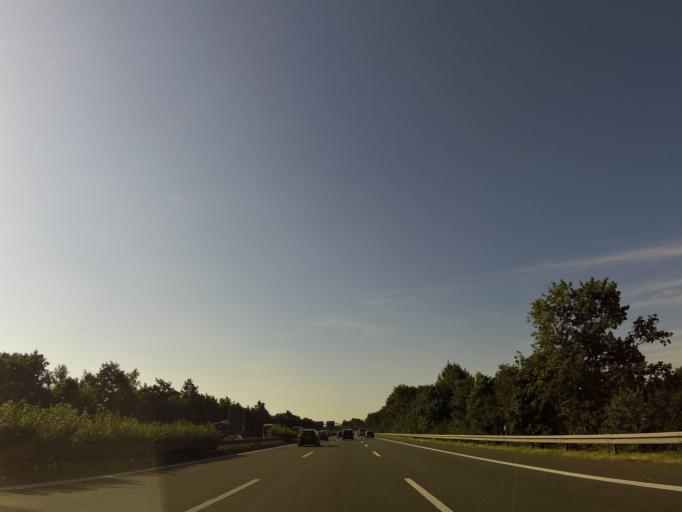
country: DE
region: Bavaria
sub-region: Regierungsbezirk Mittelfranken
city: Erlangen
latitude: 49.5504
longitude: 11.0117
